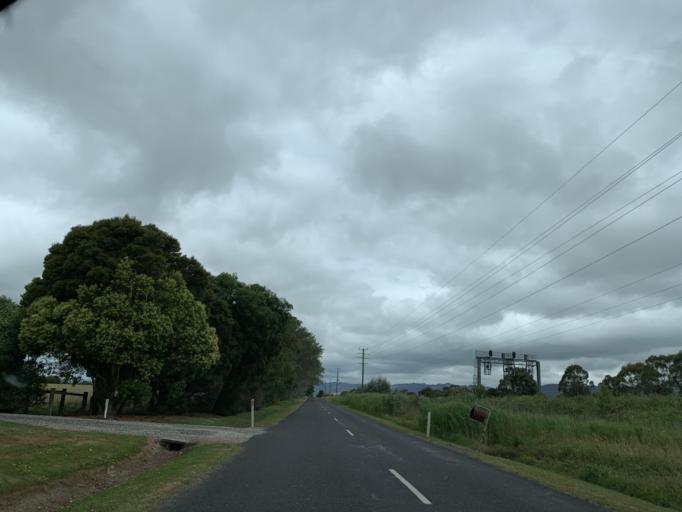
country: AU
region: Victoria
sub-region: Baw Baw
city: Warragul
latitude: -38.2043
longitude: 146.0803
